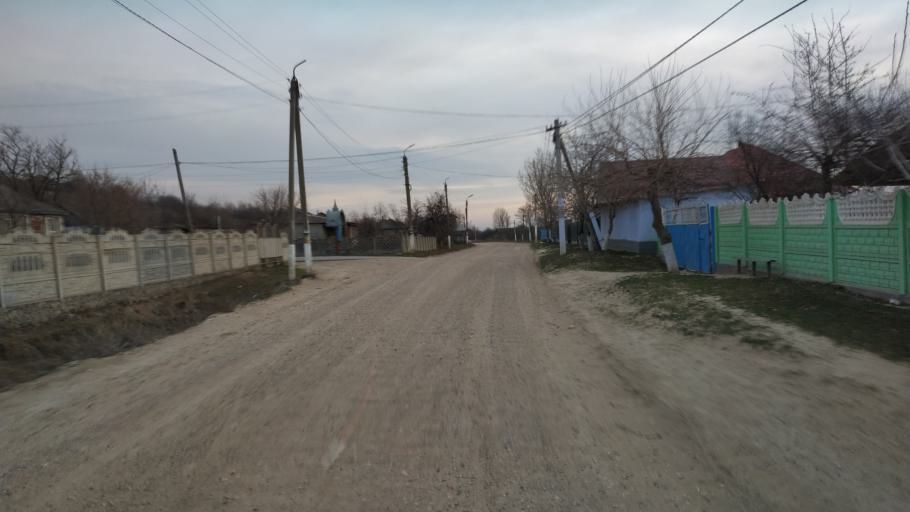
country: MD
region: Hincesti
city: Dancu
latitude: 46.7513
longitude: 28.2063
